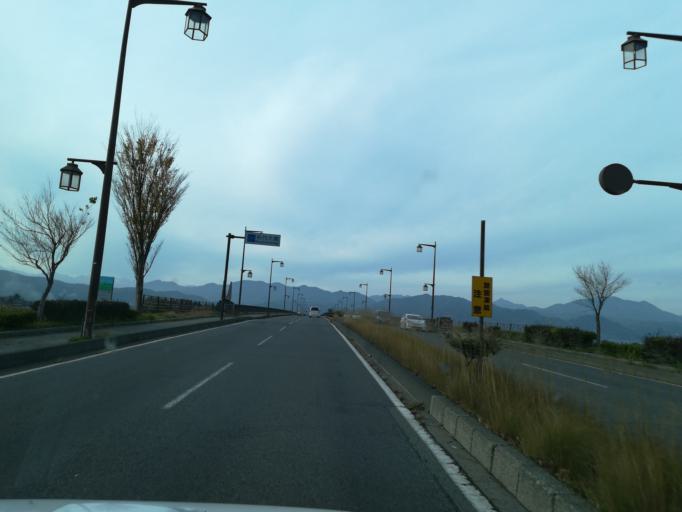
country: JP
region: Nagano
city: Nagano-shi
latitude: 36.5791
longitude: 138.1965
